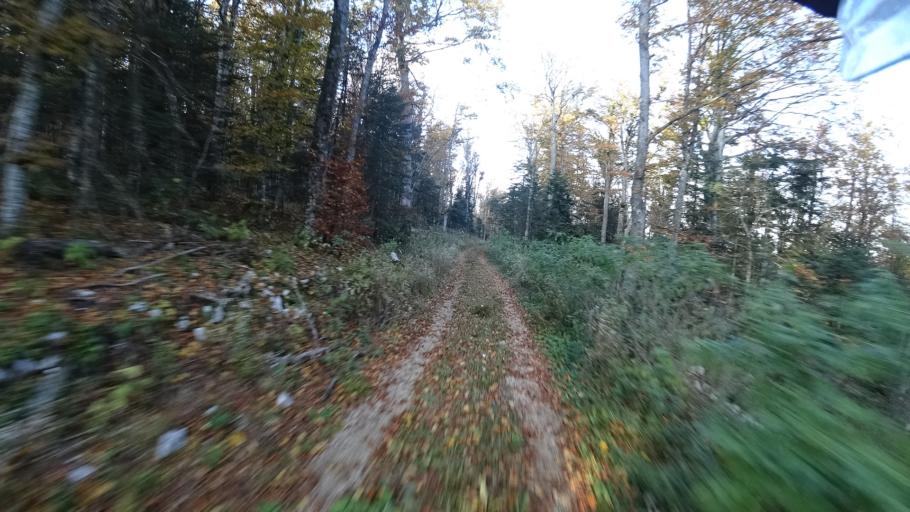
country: HR
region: Karlovacka
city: Plaski
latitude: 44.9513
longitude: 15.4062
